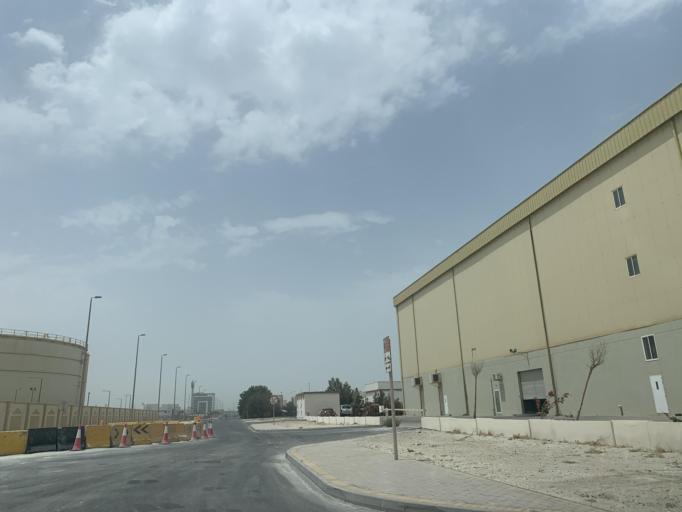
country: BH
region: Muharraq
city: Al Hadd
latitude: 26.2234
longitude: 50.6827
